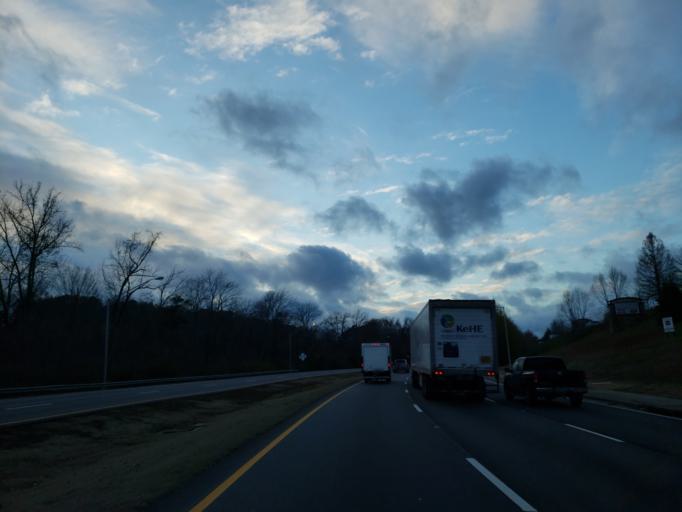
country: US
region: Georgia
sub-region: Fulton County
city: College Park
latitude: 33.6541
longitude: -84.5063
